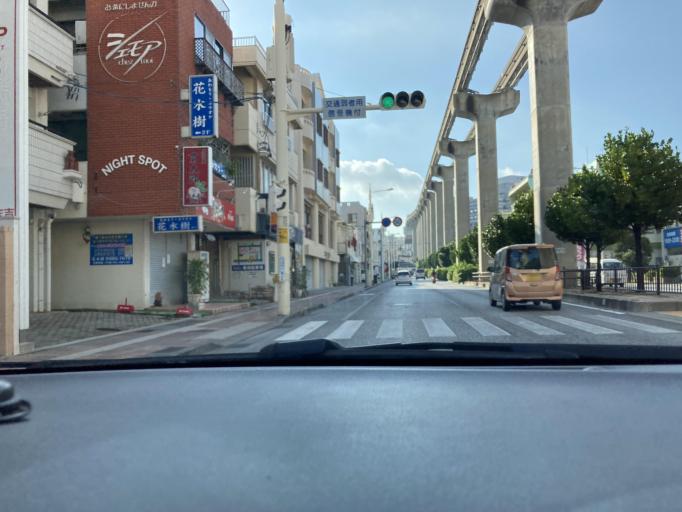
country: JP
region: Okinawa
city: Naha-shi
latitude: 26.2295
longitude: 127.7075
